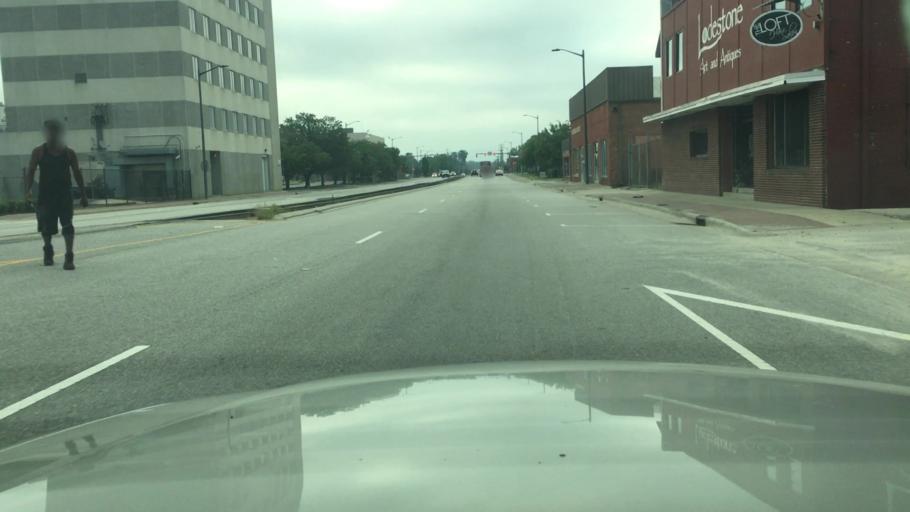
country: US
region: North Carolina
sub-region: Cumberland County
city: Fayetteville
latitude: 35.0514
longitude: -78.8817
